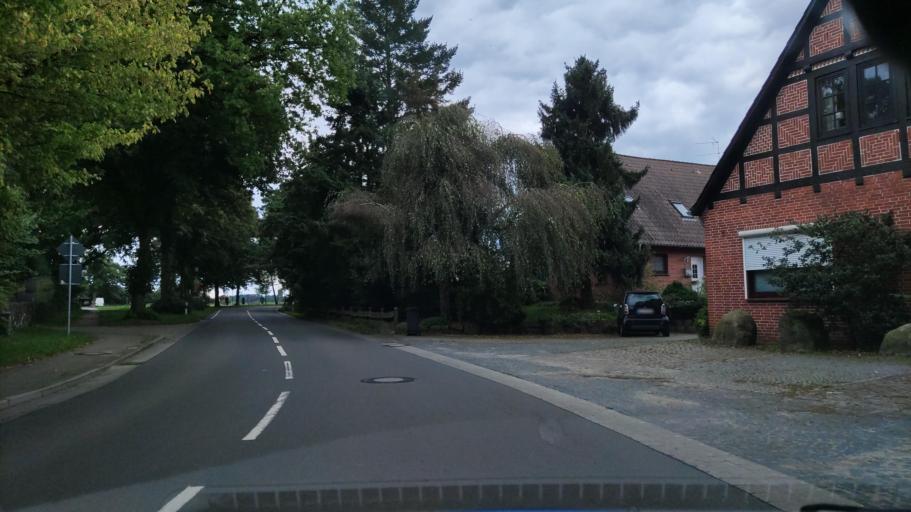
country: DE
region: Lower Saxony
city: Dohren
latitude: 53.3029
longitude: 9.7032
